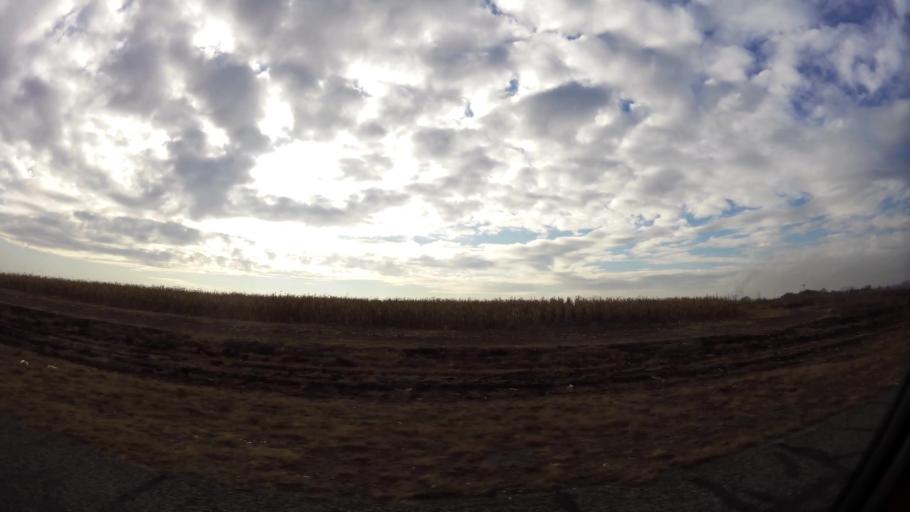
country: ZA
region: Gauteng
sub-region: Sedibeng District Municipality
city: Vanderbijlpark
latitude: -26.6480
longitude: 27.7791
